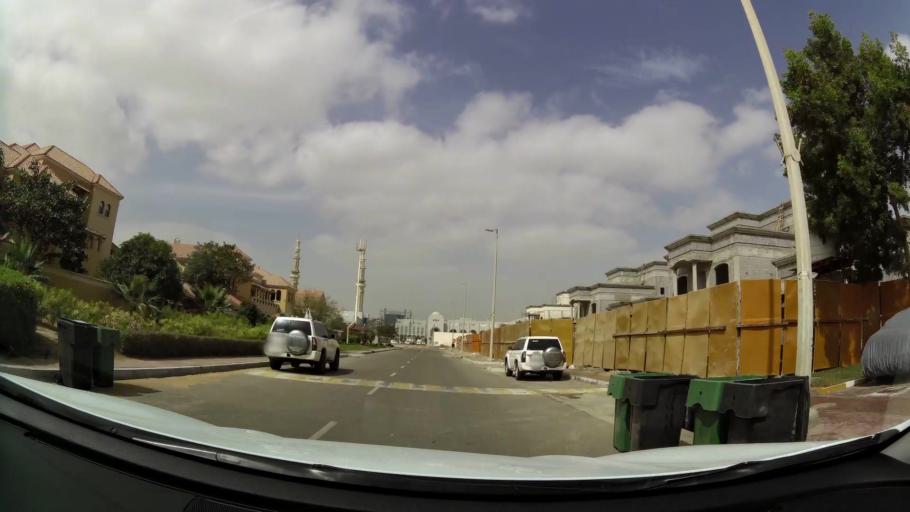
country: AE
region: Abu Dhabi
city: Abu Dhabi
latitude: 24.4064
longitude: 54.5084
